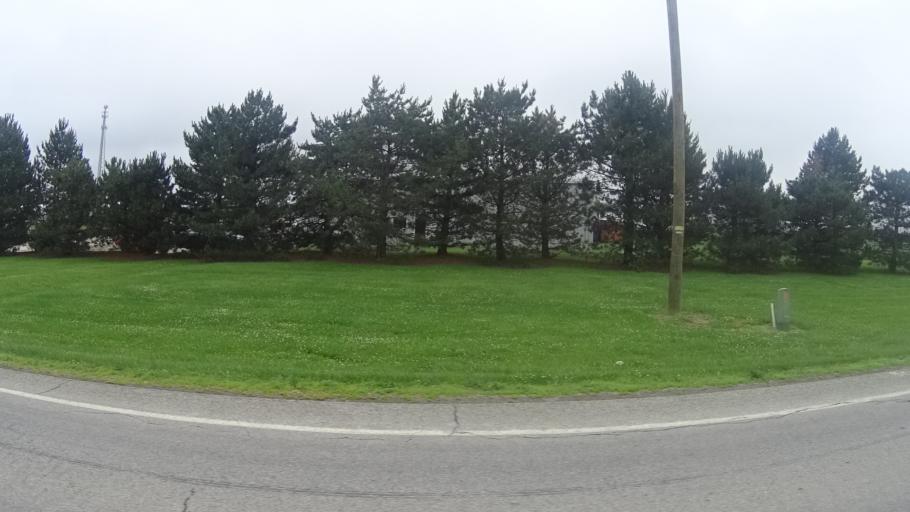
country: US
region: Ohio
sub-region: Erie County
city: Milan
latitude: 41.3335
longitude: -82.6049
